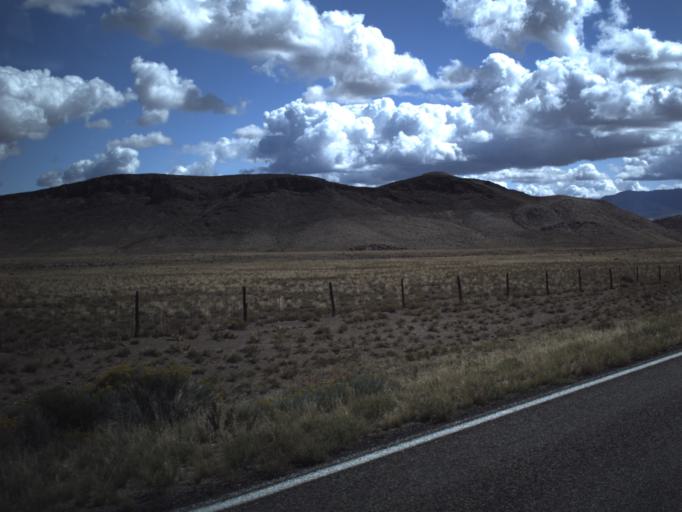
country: US
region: Utah
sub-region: Beaver County
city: Milford
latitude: 38.5970
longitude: -113.8270
